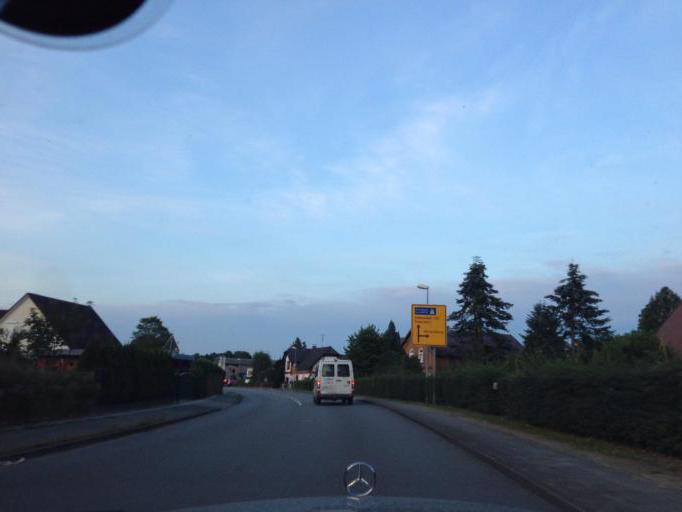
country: DE
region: Schleswig-Holstein
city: Hammoor
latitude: 53.7136
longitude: 10.3245
